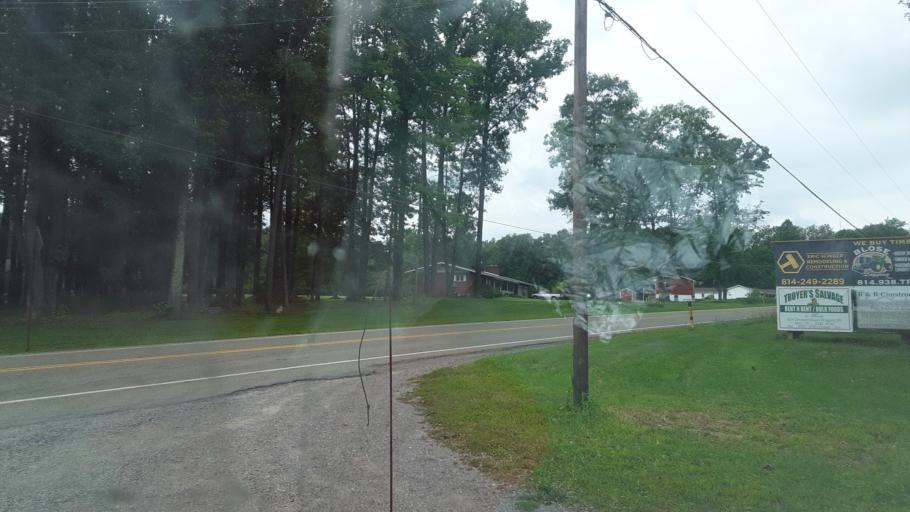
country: US
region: Pennsylvania
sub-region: Jefferson County
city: Punxsutawney
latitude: 40.9745
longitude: -79.1066
